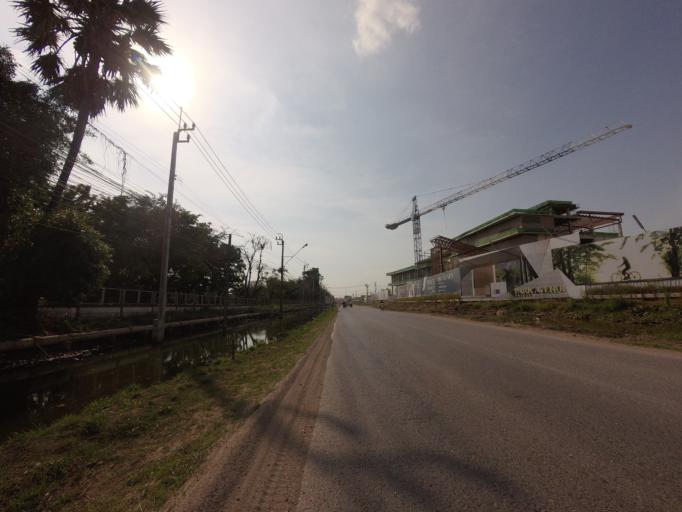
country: TH
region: Bangkok
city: Suan Luang
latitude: 13.7465
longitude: 100.6621
